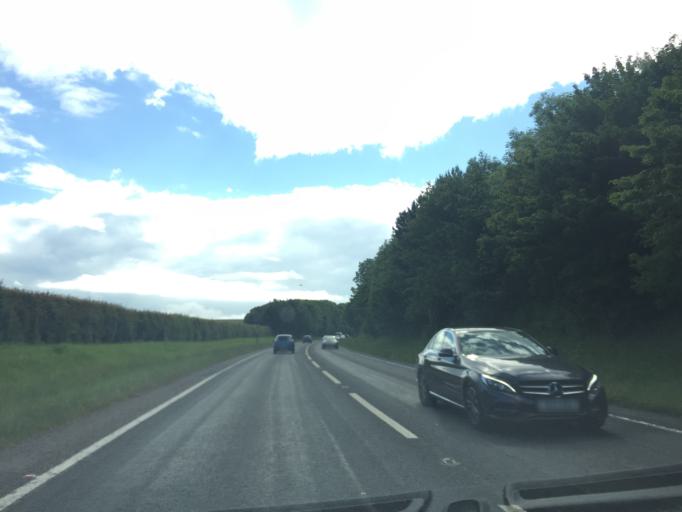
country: GB
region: England
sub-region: Dorset
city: Dorchester
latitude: 50.7020
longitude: -2.4294
